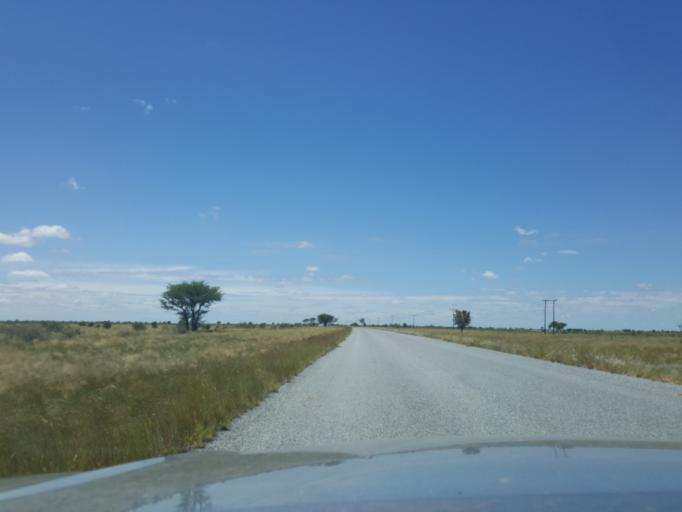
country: BW
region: Central
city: Nata
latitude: -20.1946
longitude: 26.0921
